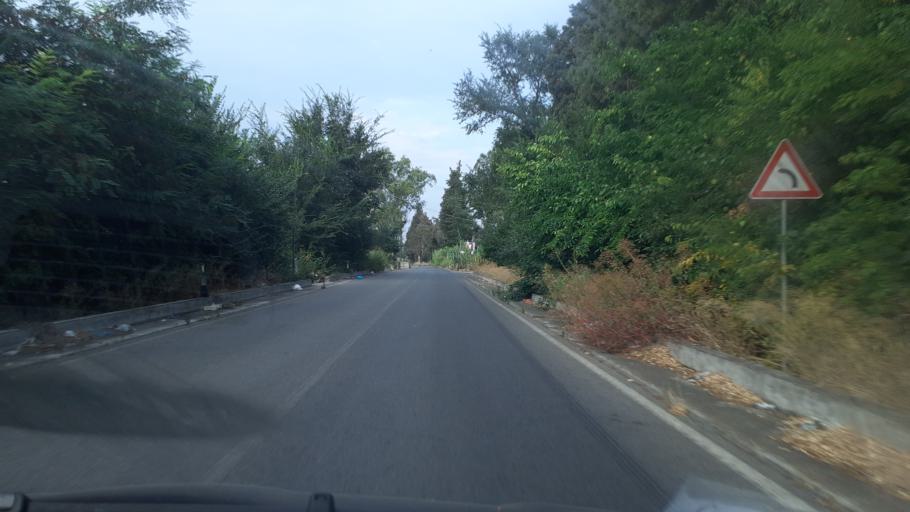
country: IT
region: Sicily
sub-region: Catania
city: Catania
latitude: 37.4529
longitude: 15.0264
